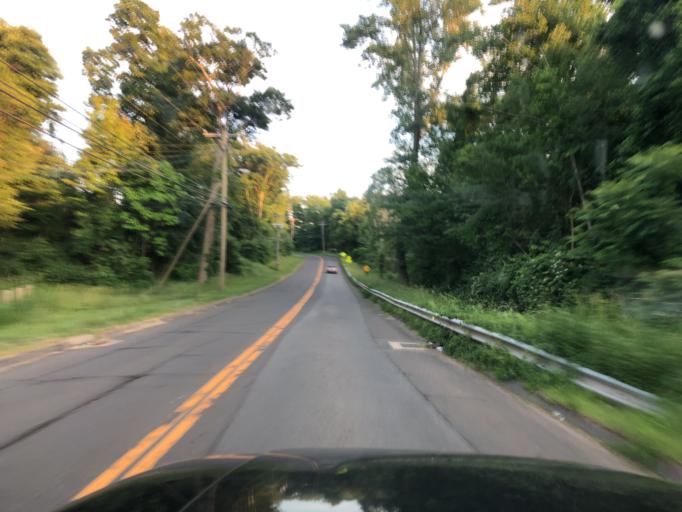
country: US
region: Connecticut
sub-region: Middlesex County
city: Middletown
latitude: 41.5644
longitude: -72.7140
